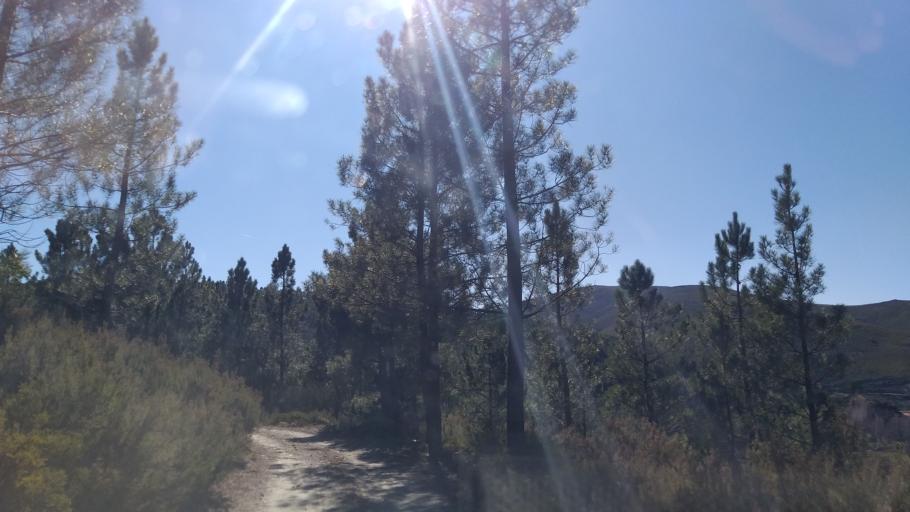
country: PT
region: Guarda
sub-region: Manteigas
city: Manteigas
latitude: 40.4457
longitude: -7.5086
